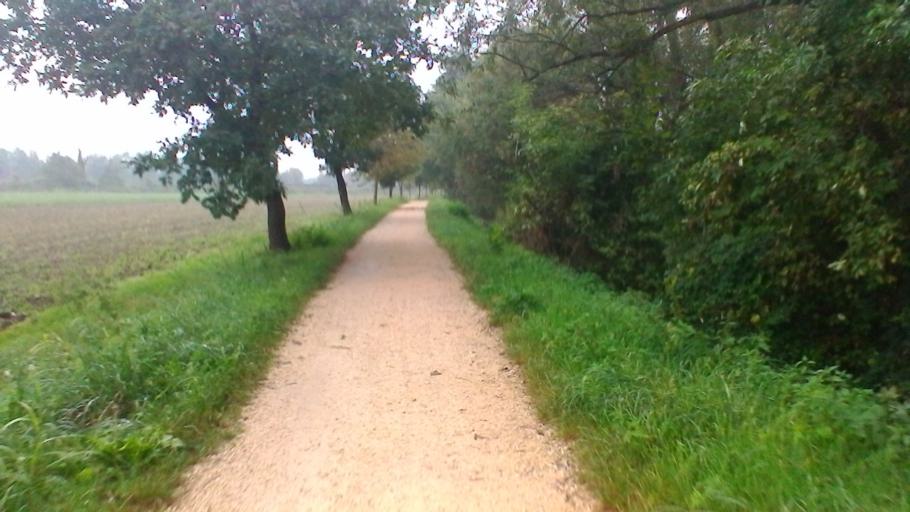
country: IT
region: Veneto
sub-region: Provincia di Verona
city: Montorio
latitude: 45.4286
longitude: 11.0380
